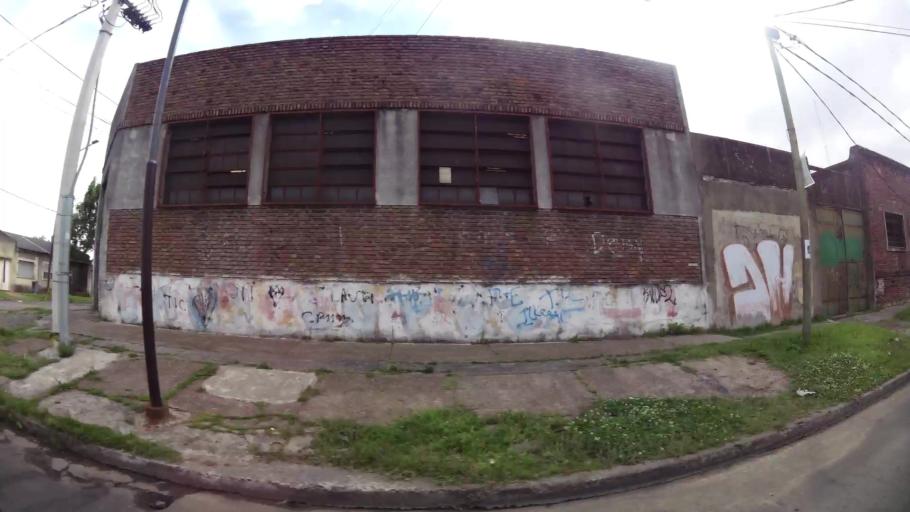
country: AR
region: Buenos Aires
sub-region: Partido de Lanus
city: Lanus
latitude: -34.6958
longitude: -58.3804
